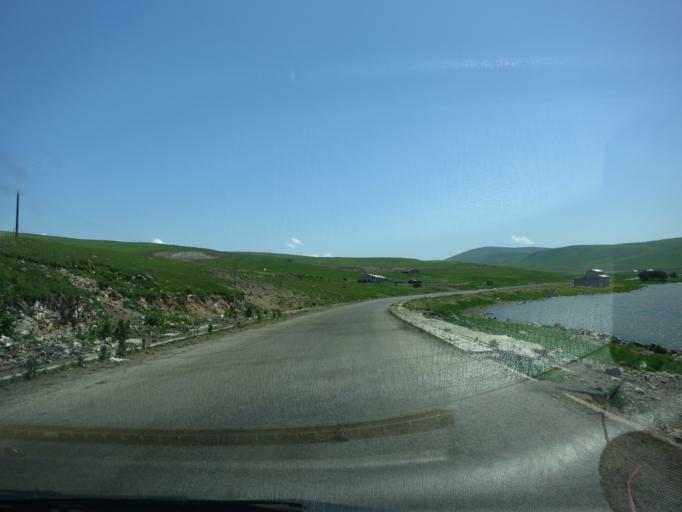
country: GE
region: Samtskhe-Javakheti
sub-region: Ninotsminda
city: Ninotsminda
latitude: 41.3077
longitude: 43.7605
